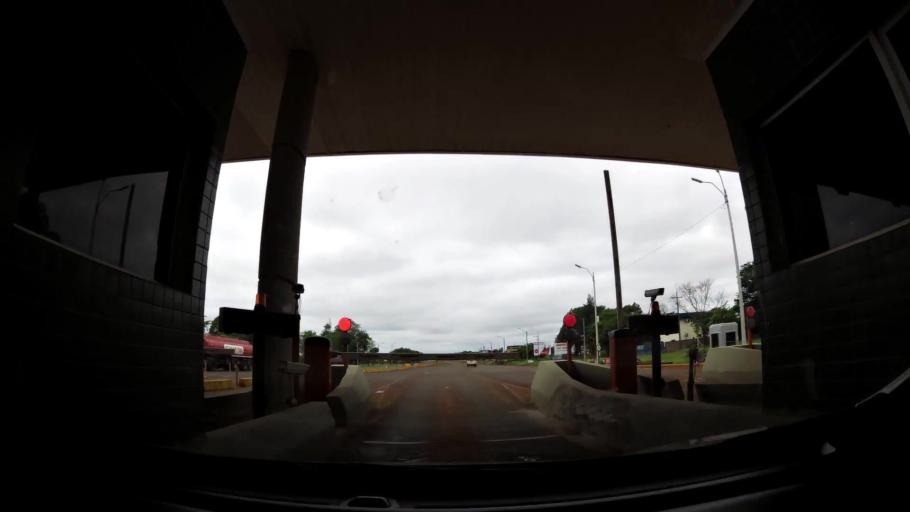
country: PY
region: Alto Parana
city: Colonia Yguazu
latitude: -25.4868
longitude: -54.8543
